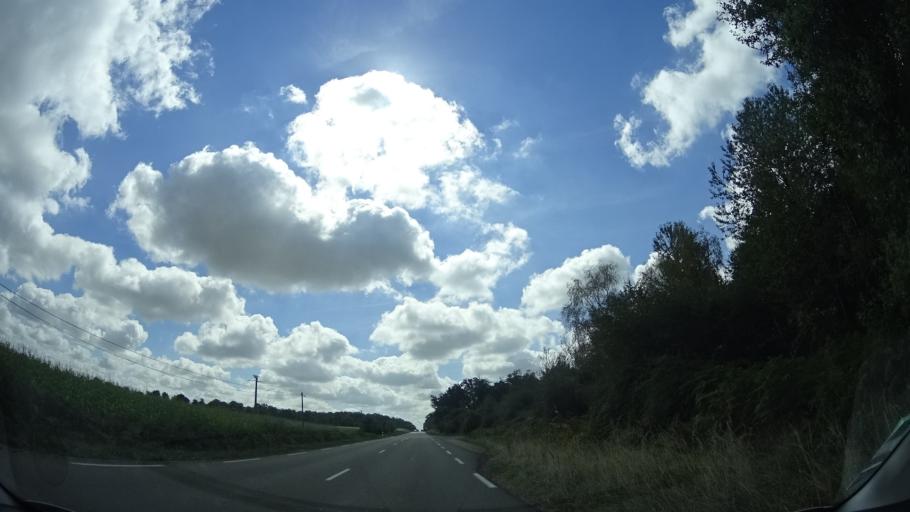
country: FR
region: Pays de la Loire
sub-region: Departement de la Mayenne
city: Meslay-du-Maine
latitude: 47.9875
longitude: -0.6222
